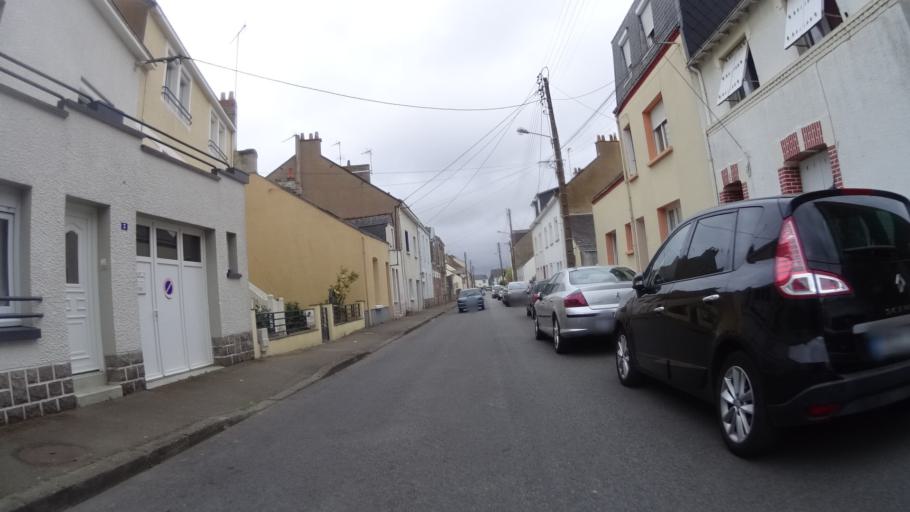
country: FR
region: Pays de la Loire
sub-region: Departement de la Loire-Atlantique
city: Saint-Nazaire
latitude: 47.2990
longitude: -2.1890
